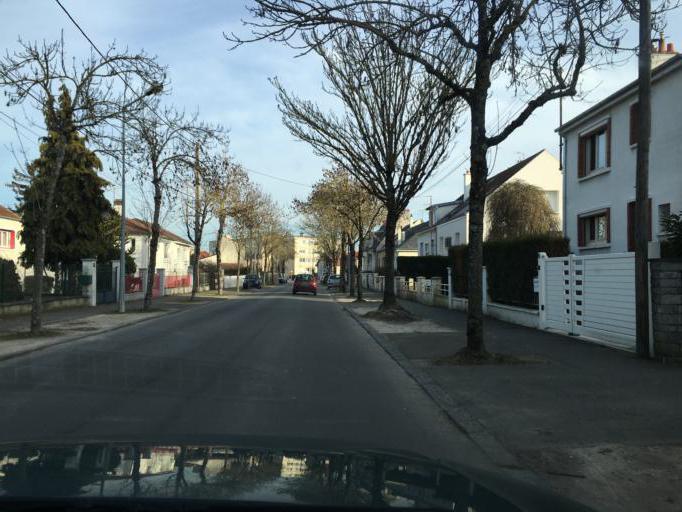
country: FR
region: Centre
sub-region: Departement du Loiret
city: Saint-Jean-le-Blanc
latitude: 47.8882
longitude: 1.9111
